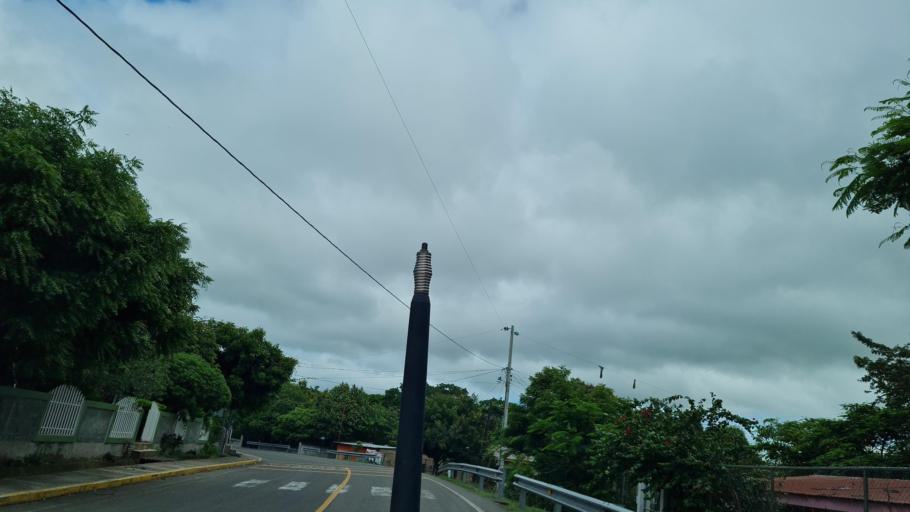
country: NI
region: Boaco
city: San Jose de los Remates
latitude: 12.5916
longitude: -85.9093
